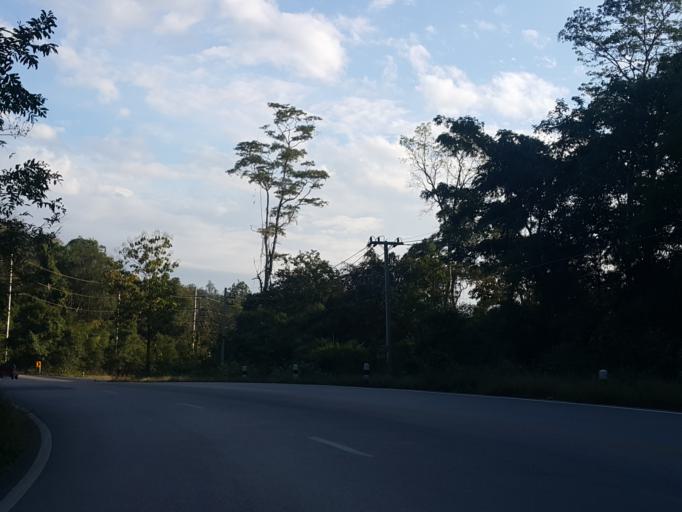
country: TH
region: Lampang
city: Chae Hom
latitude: 18.5014
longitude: 99.5477
